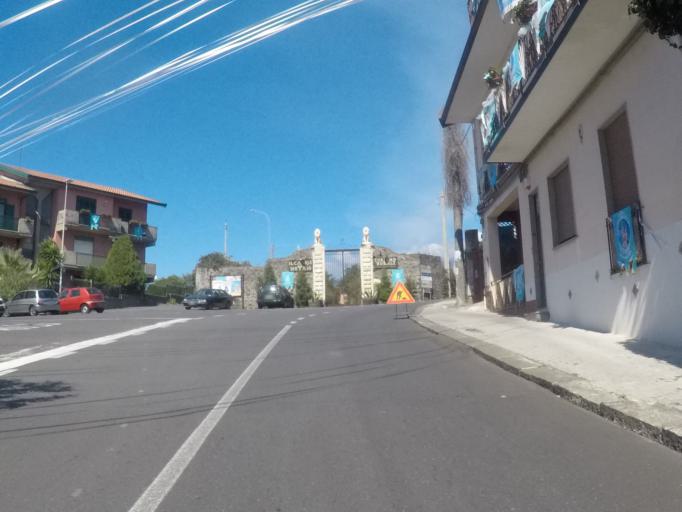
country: IT
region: Sicily
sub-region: Catania
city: Belpasso
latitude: 37.6056
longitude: 14.9846
